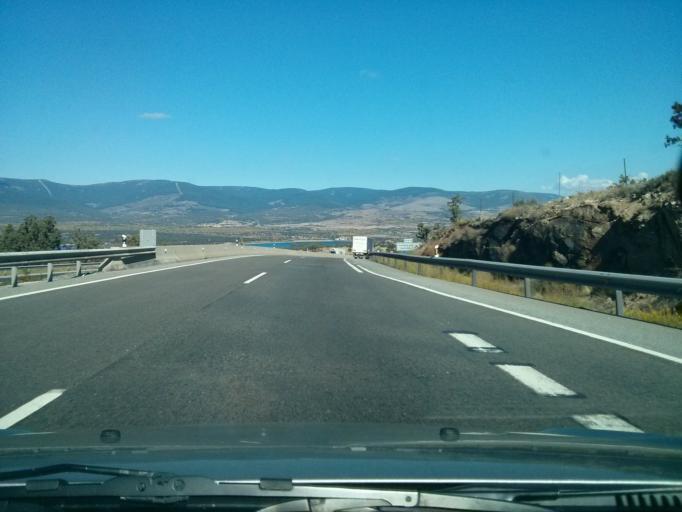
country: ES
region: Madrid
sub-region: Provincia de Madrid
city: Buitrago del Lozoya
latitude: 40.9565
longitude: -3.6412
